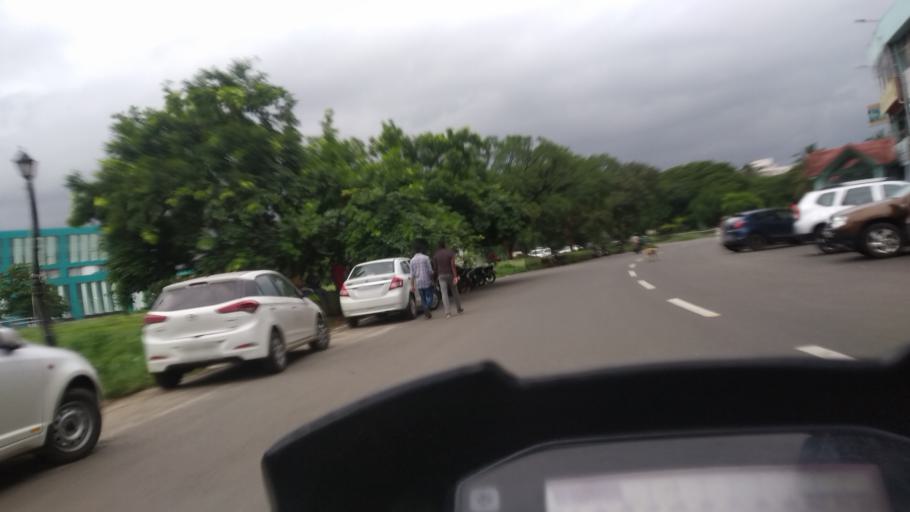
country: IN
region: Kerala
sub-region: Ernakulam
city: Cochin
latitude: 9.9977
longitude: 76.2998
